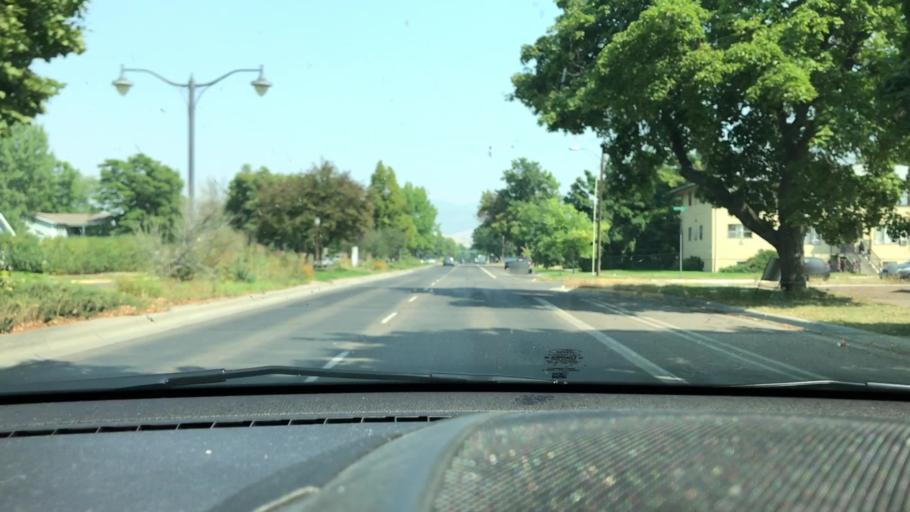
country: US
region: Montana
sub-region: Missoula County
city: Missoula
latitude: 46.8587
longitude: -114.0096
